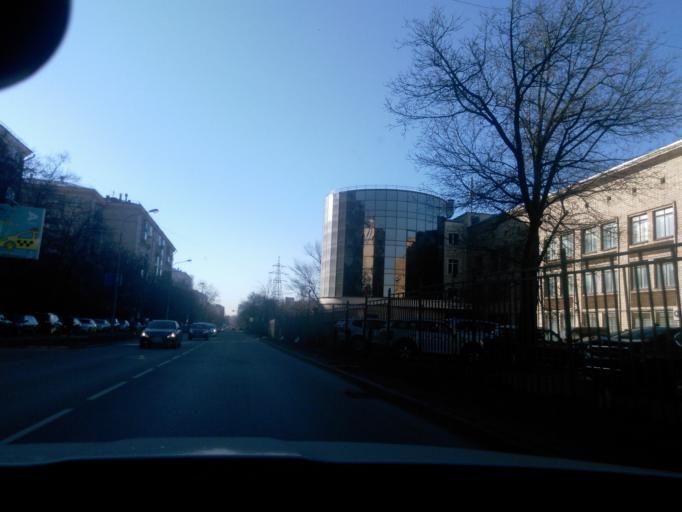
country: RU
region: Moscow
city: Sokol
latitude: 55.7860
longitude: 37.5095
